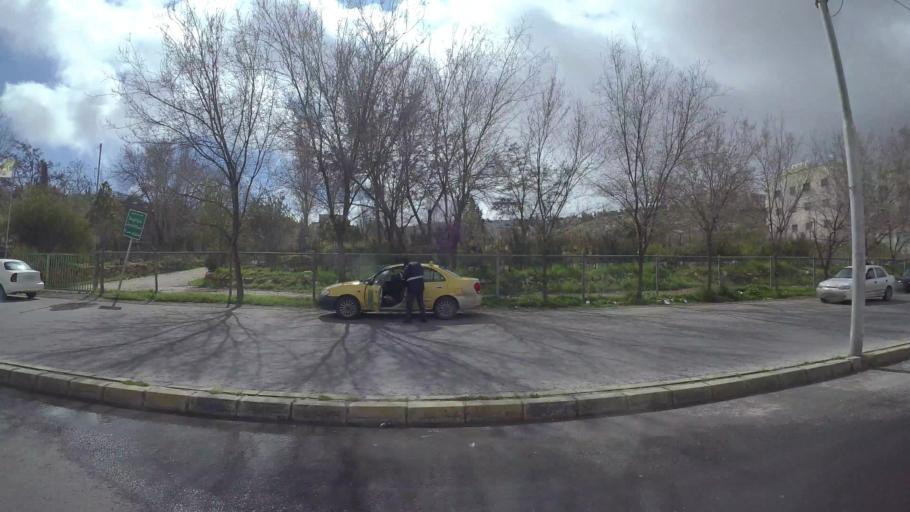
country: JO
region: Amman
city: Al Jubayhah
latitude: 32.0626
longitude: 35.8829
